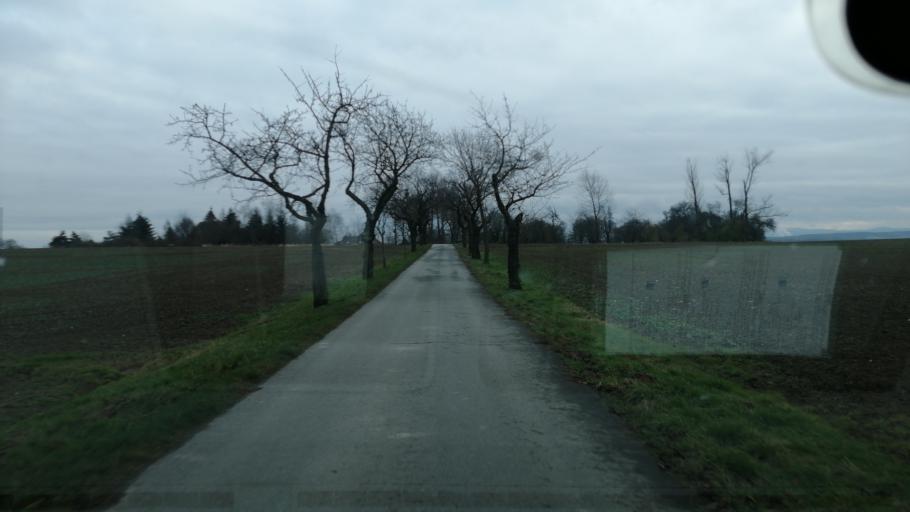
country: DE
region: Saxony
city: Bernstadt
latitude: 51.0540
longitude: 14.7907
